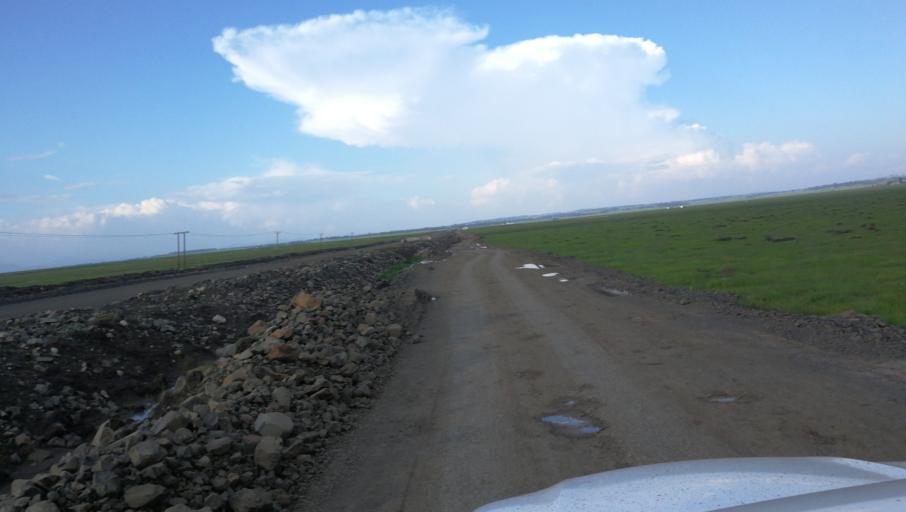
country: ET
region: Amhara
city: Were Ilu
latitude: 10.4816
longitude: 39.2992
